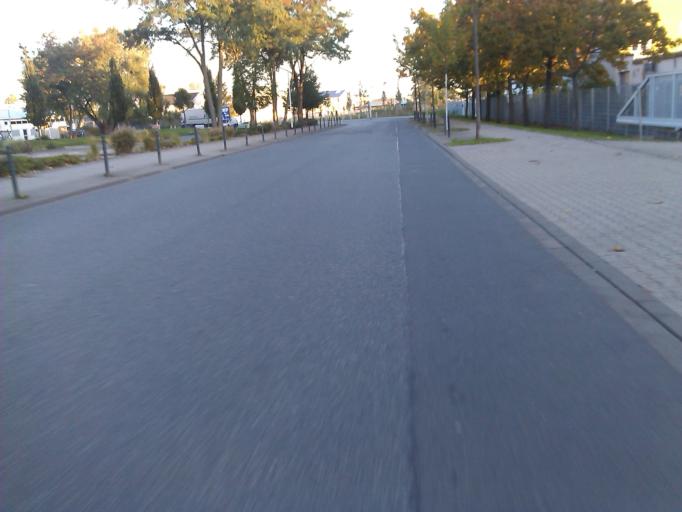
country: DE
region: Hesse
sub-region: Regierungsbezirk Darmstadt
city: Darmstadt
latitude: 49.8851
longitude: 8.6422
